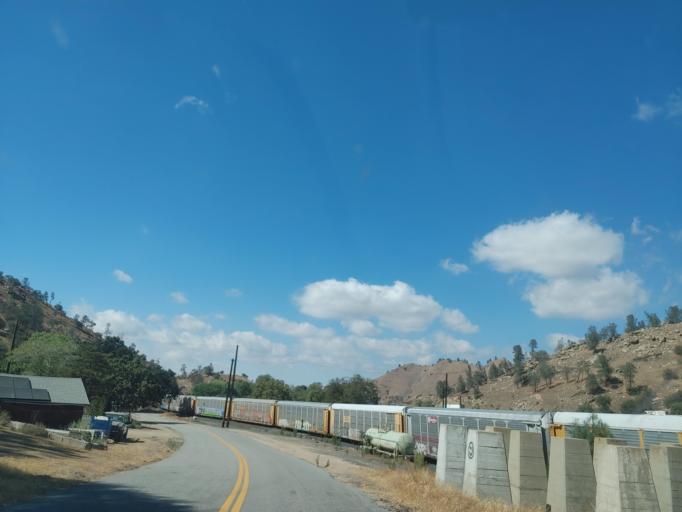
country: US
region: California
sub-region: Kern County
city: Bear Valley Springs
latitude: 35.2165
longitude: -118.5553
